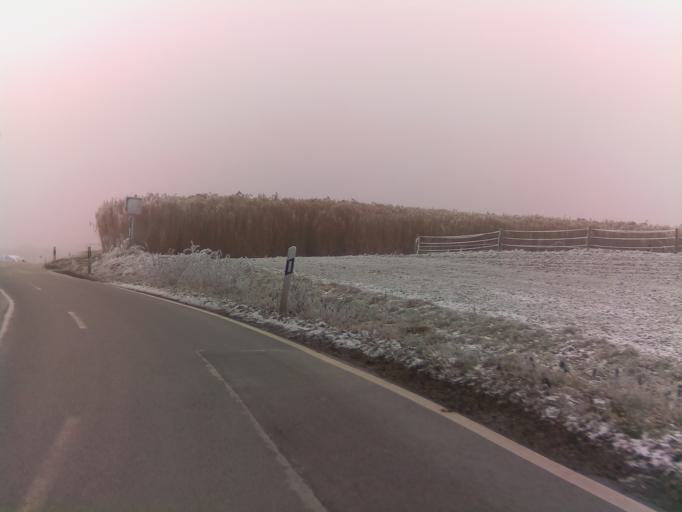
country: DE
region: Hesse
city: Lutzelbach
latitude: 49.7358
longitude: 8.7264
